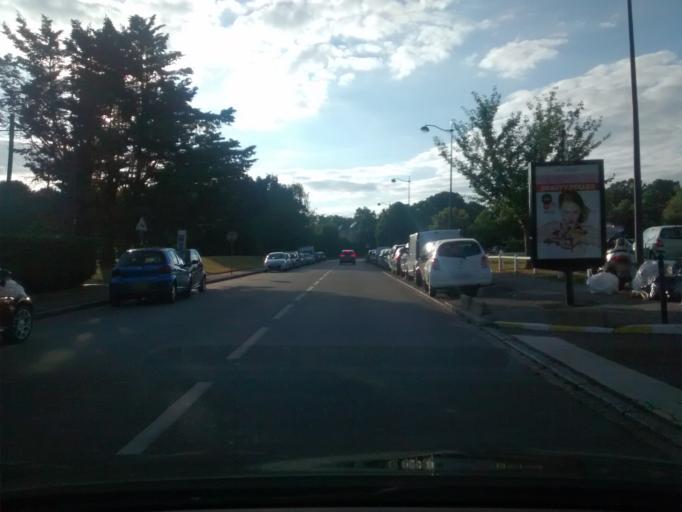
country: FR
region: Ile-de-France
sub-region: Departement des Yvelines
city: Le Chesnay
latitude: 48.8210
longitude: 2.1179
